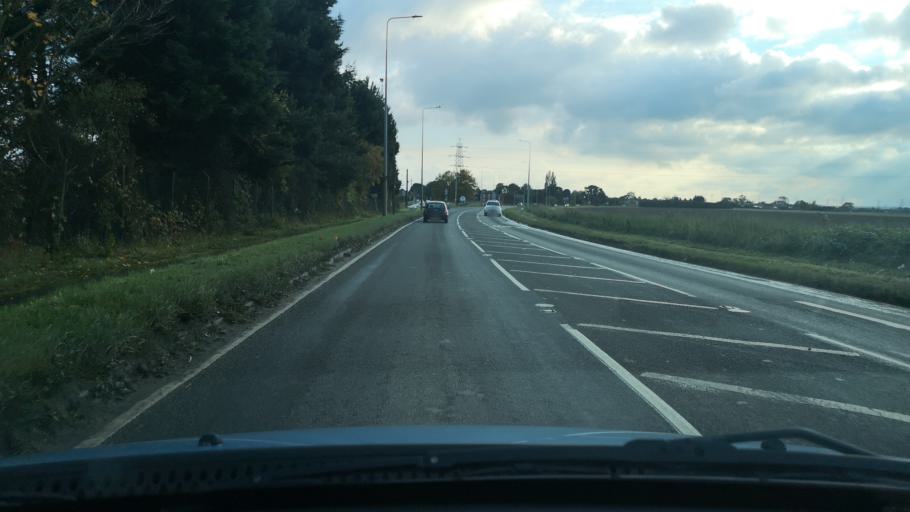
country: GB
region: England
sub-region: North Lincolnshire
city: Gunness
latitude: 53.5846
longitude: -0.7370
